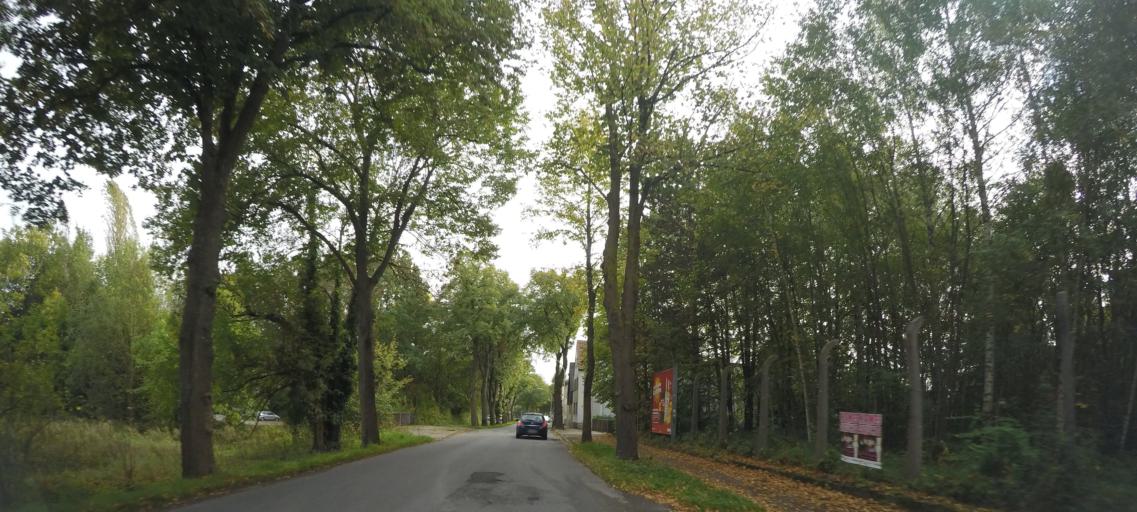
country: DE
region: North Rhine-Westphalia
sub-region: Regierungsbezirk Arnsberg
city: Lippstadt
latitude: 51.6679
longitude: 8.3577
